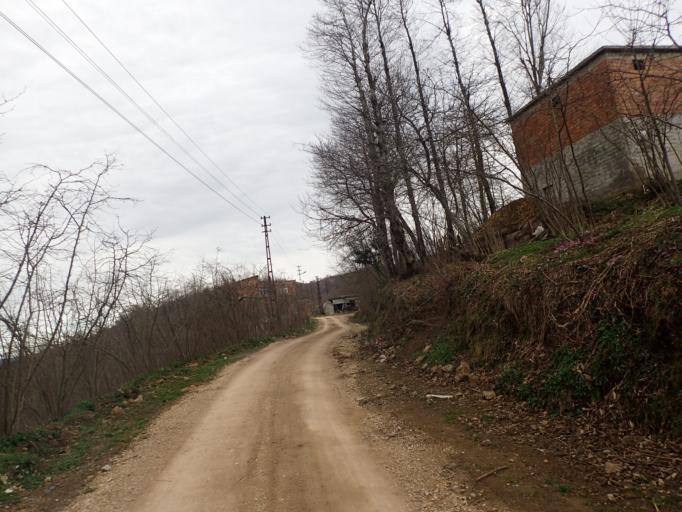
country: TR
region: Ordu
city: Camas
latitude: 40.8901
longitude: 37.5197
